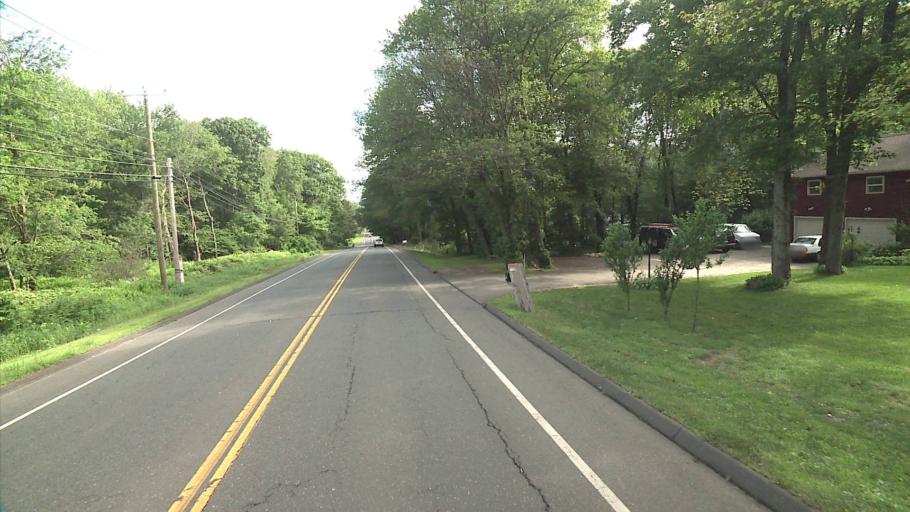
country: US
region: Connecticut
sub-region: New Haven County
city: Prospect
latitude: 41.4447
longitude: -72.9894
